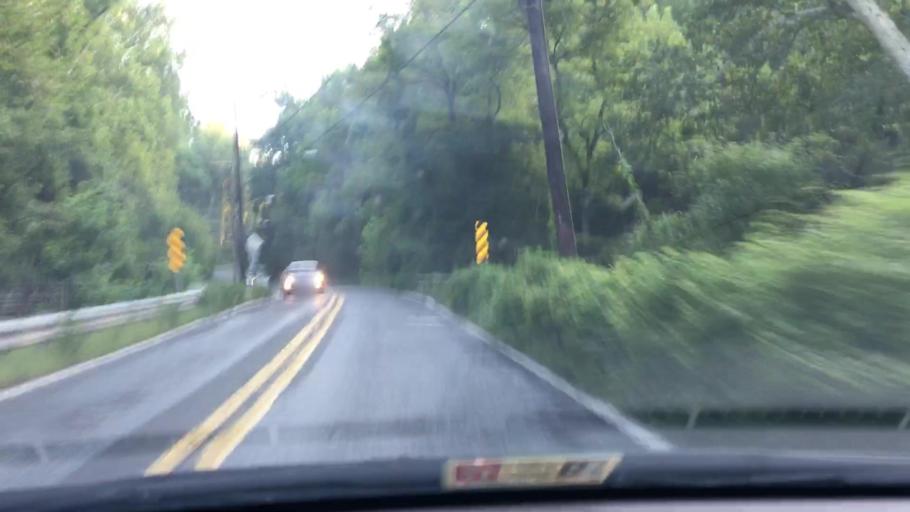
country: US
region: Maryland
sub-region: Montgomery County
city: Rockville
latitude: 39.0903
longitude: -77.1151
